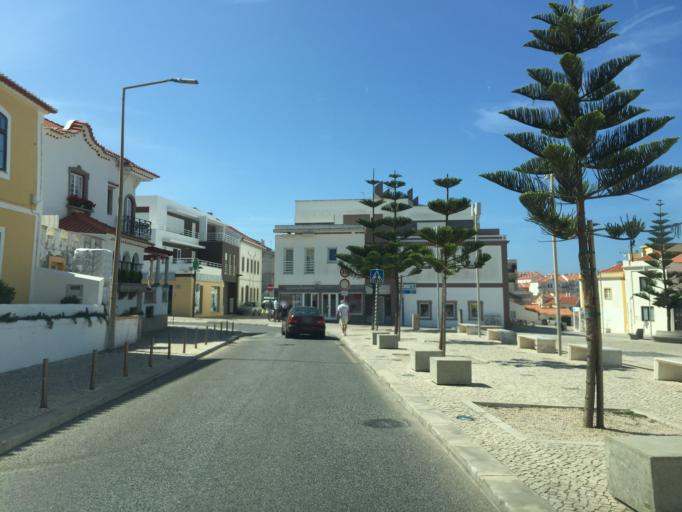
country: PT
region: Lisbon
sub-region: Torres Vedras
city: Silveira
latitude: 39.1354
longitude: -9.3815
